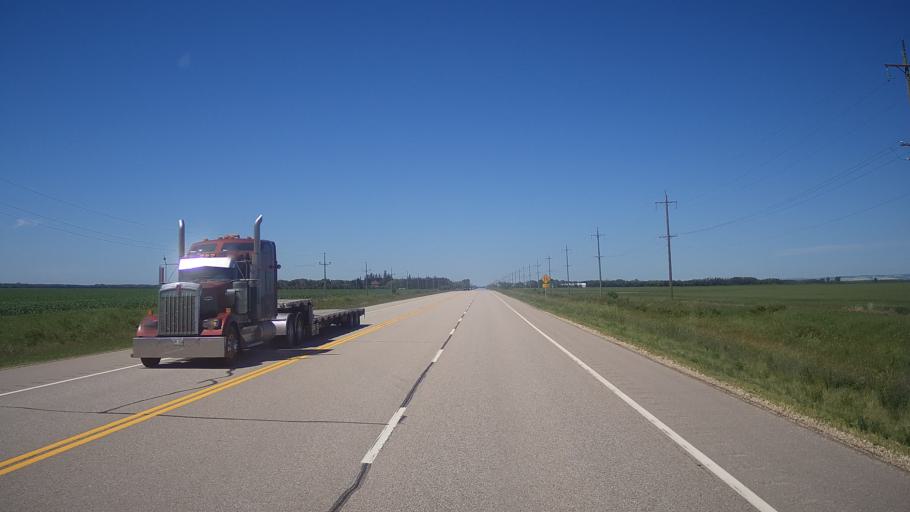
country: CA
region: Manitoba
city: Neepawa
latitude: 50.2252
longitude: -99.2949
